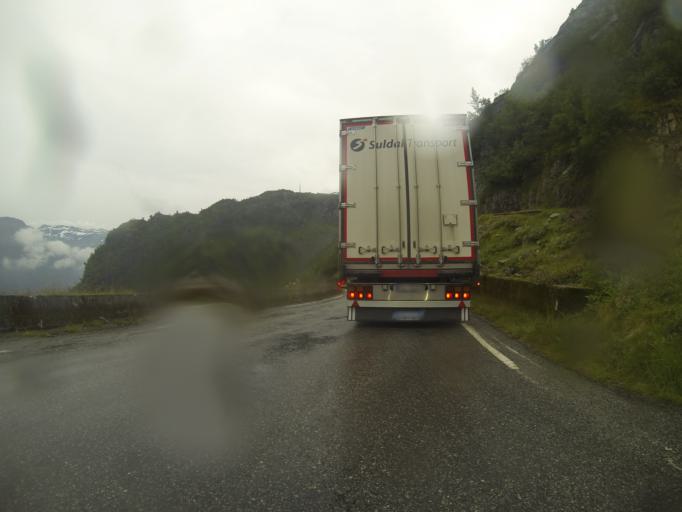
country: NO
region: Hordaland
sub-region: Odda
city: Odda
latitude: 59.7862
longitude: 6.7561
